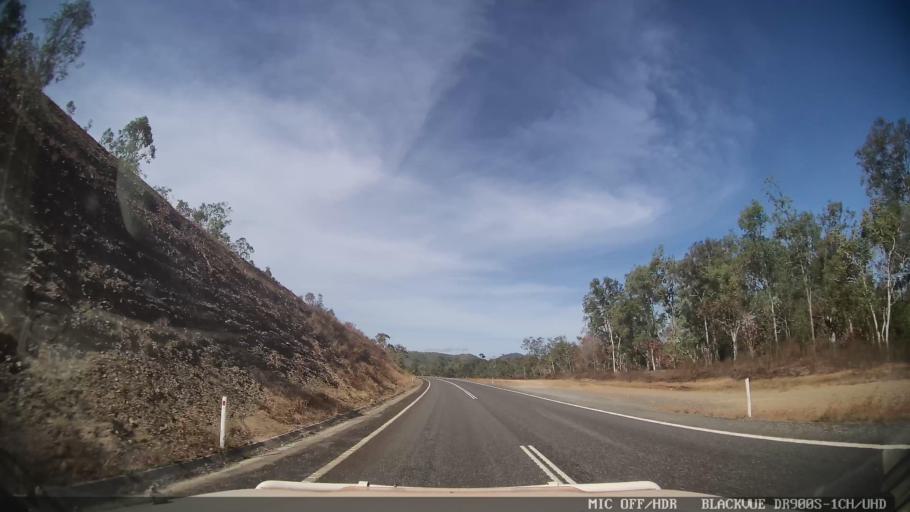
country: AU
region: Queensland
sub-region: Cook
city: Cooktown
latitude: -15.6796
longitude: 145.1720
